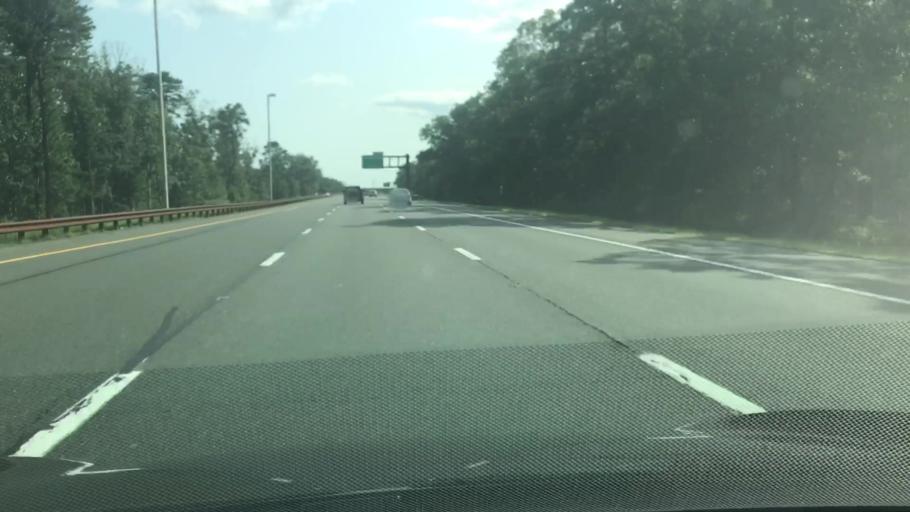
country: US
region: New Jersey
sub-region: Ocean County
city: Forked River
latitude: 39.8695
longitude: -74.2172
